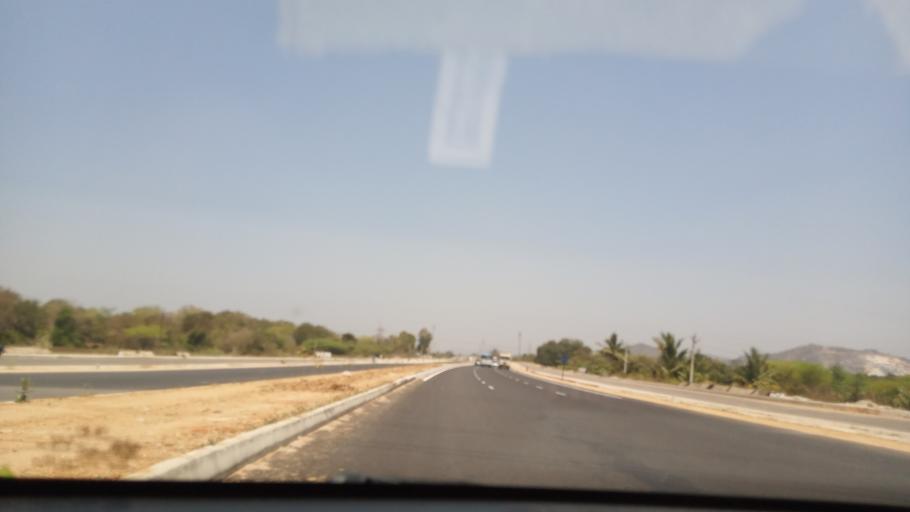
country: IN
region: Andhra Pradesh
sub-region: Chittoor
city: Pakala
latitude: 13.4117
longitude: 79.1114
